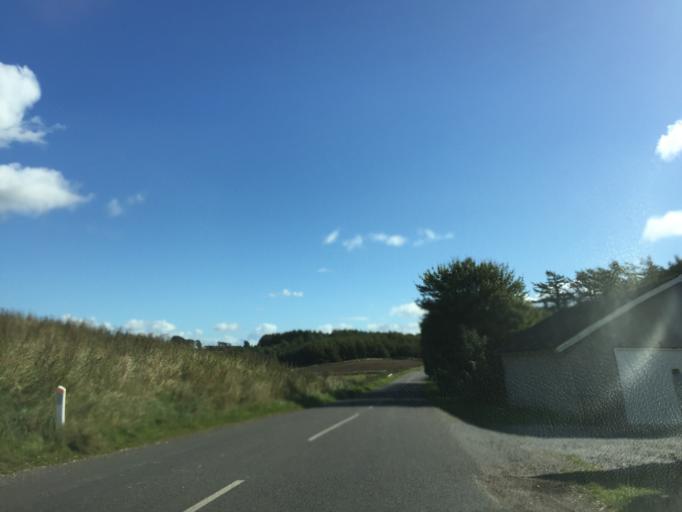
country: DK
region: Central Jutland
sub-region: Viborg Kommune
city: Bjerringbro
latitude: 56.4064
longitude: 9.6176
